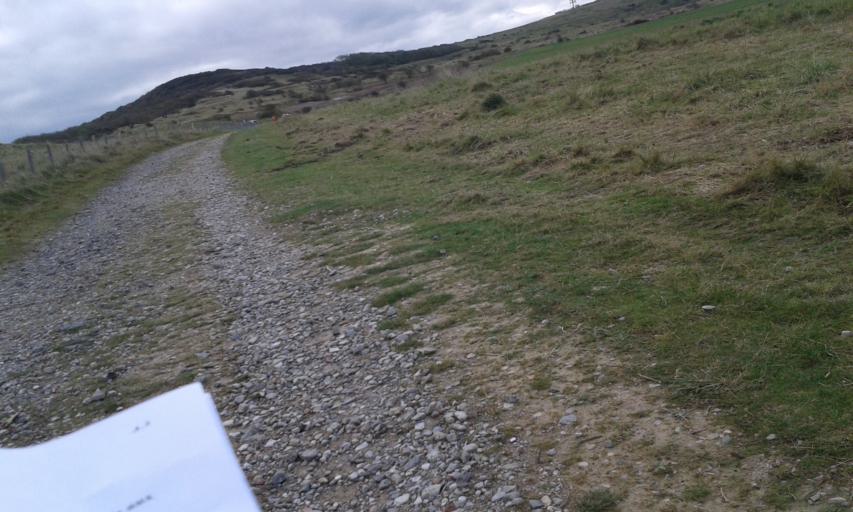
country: FR
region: Nord-Pas-de-Calais
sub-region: Departement du Pas-de-Calais
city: Sangatte
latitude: 50.9320
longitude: 1.7297
